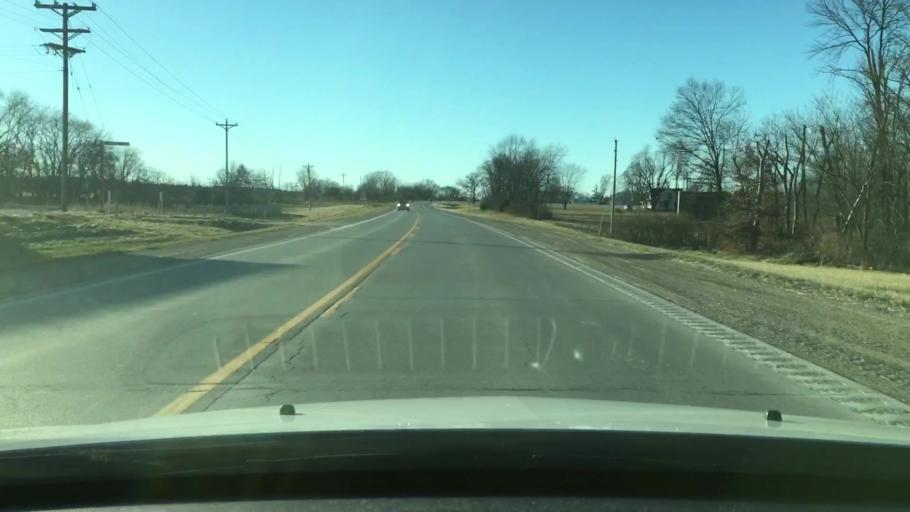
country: US
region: Missouri
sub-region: Audrain County
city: Mexico
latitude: 39.1900
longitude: -91.9834
